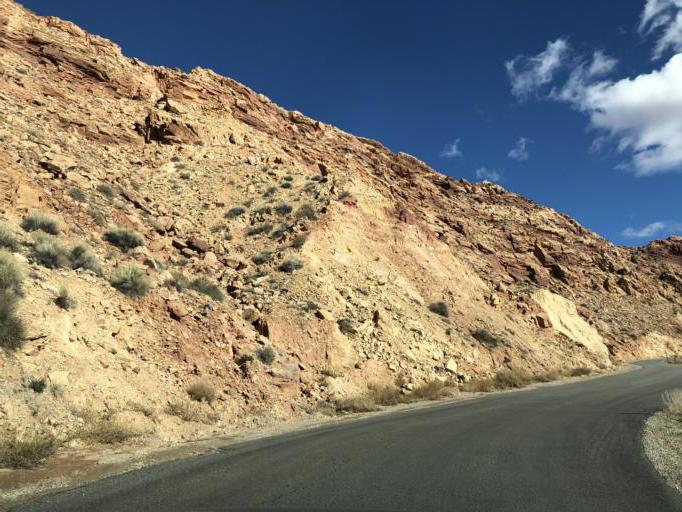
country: US
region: Utah
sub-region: Grand County
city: Moab
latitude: 38.5891
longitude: -109.5569
